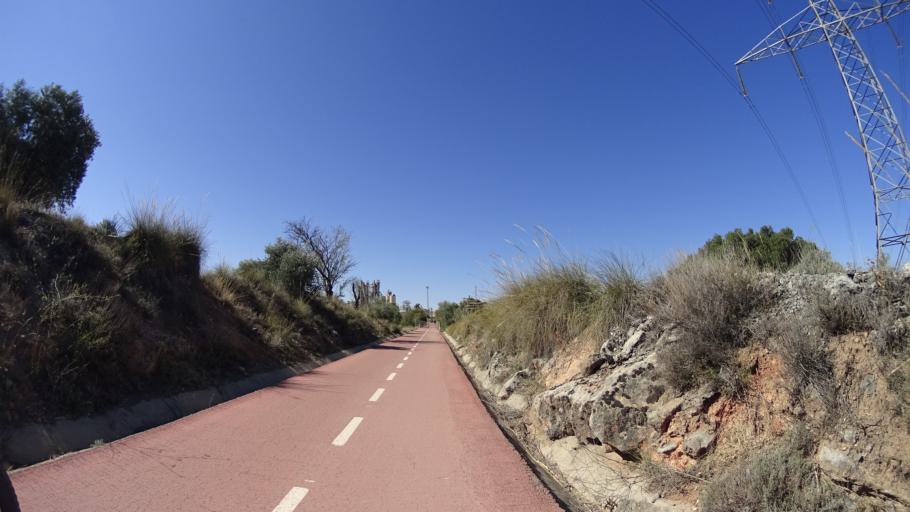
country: ES
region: Madrid
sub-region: Provincia de Madrid
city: Morata de Tajuna
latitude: 40.2546
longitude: -3.4732
